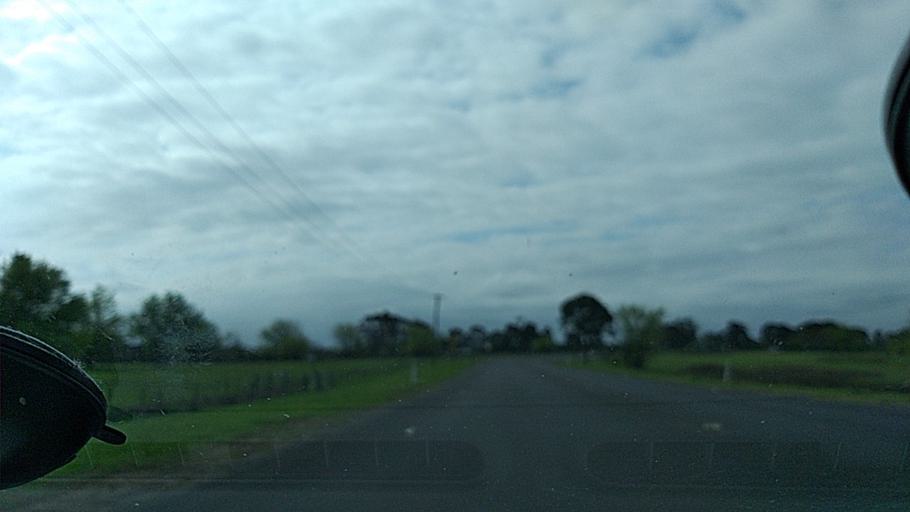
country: AU
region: New South Wales
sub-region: Campbelltown Municipality
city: Glen Alpine
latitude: -34.1155
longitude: 150.7438
